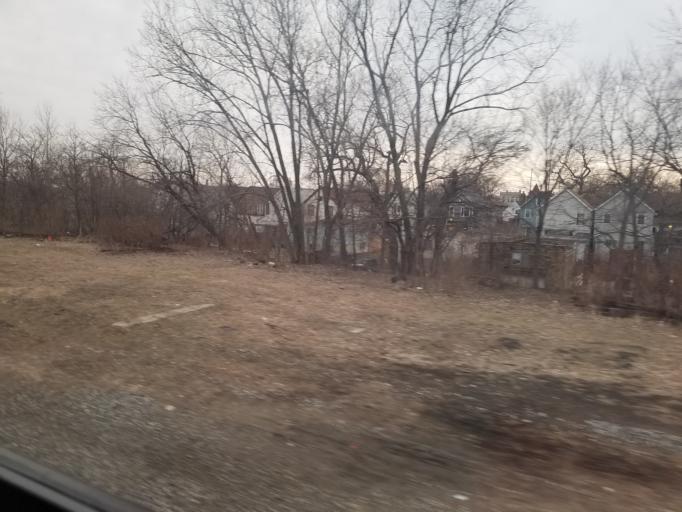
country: US
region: Illinois
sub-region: Cook County
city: Chicago
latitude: 41.7922
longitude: -87.6354
